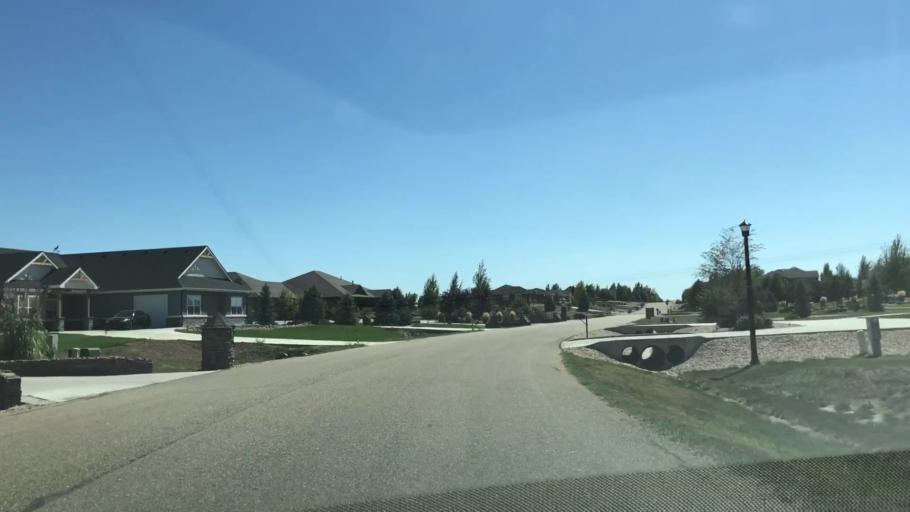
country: US
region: Colorado
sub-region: Weld County
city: Windsor
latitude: 40.4478
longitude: -104.9464
